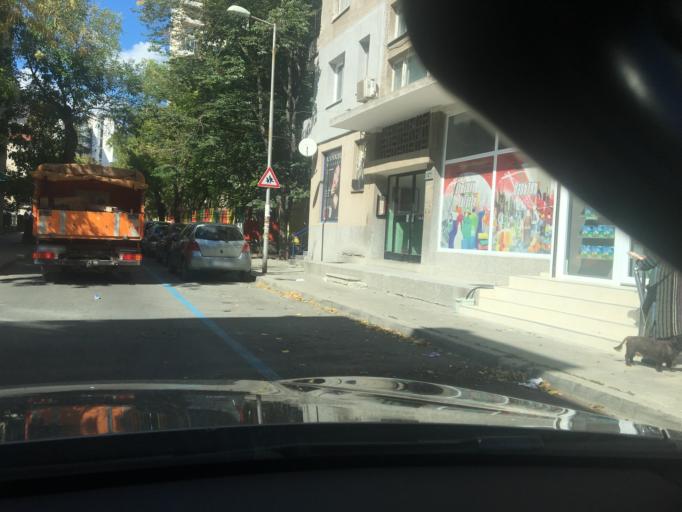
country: BG
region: Burgas
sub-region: Obshtina Burgas
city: Burgas
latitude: 42.5018
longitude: 27.4728
